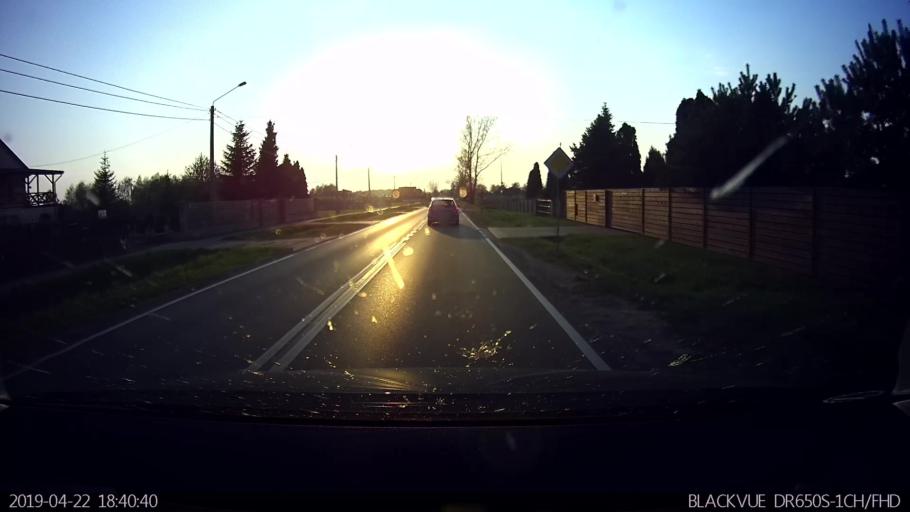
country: PL
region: Masovian Voivodeship
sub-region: Powiat wolominski
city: Dabrowka
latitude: 52.4467
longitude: 21.2737
